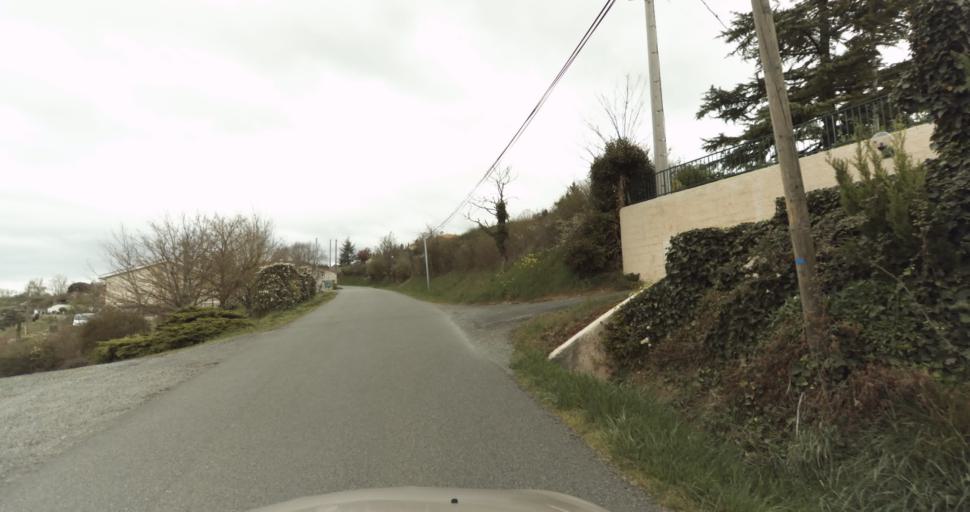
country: FR
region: Midi-Pyrenees
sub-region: Departement du Tarn
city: Puygouzon
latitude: 43.9014
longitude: 2.1611
